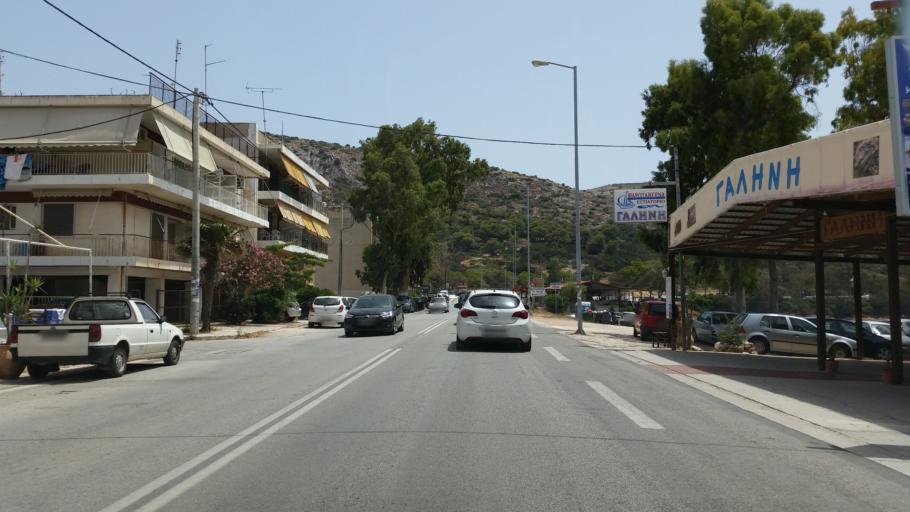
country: GR
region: Attica
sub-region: Nomarchia Anatolikis Attikis
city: Palaia Fokaia
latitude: 37.7165
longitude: 23.9459
